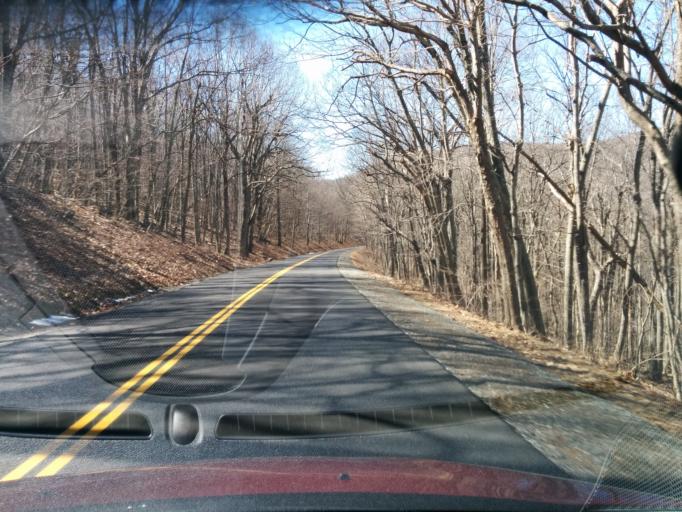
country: US
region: Virginia
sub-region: Augusta County
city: Stuarts Draft
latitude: 37.8945
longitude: -79.0395
